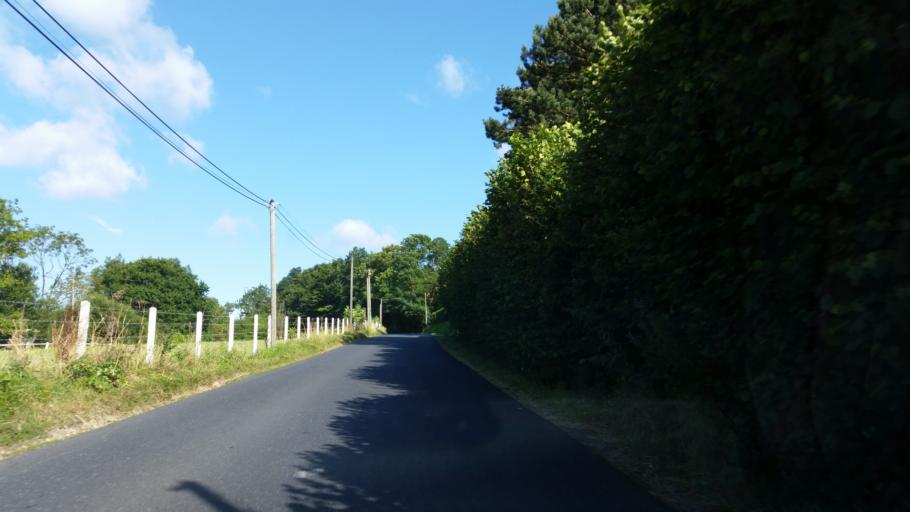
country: FR
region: Lower Normandy
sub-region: Departement du Calvados
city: Touques
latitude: 49.3382
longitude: 0.1279
